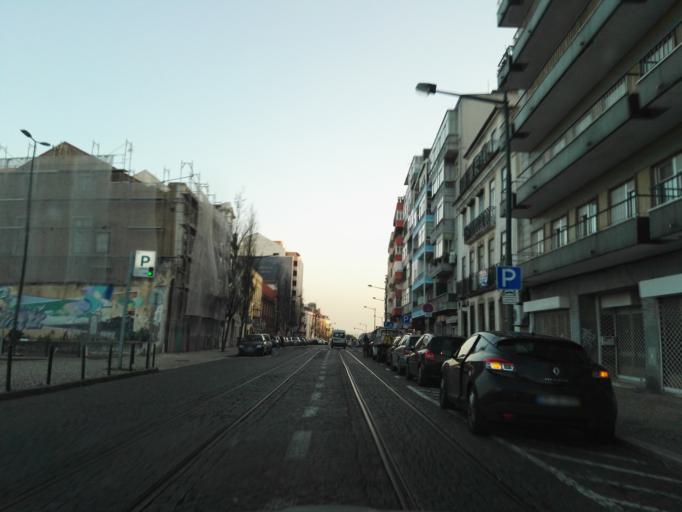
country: PT
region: Lisbon
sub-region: Lisbon
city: Lisbon
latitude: 38.7251
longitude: -9.1404
